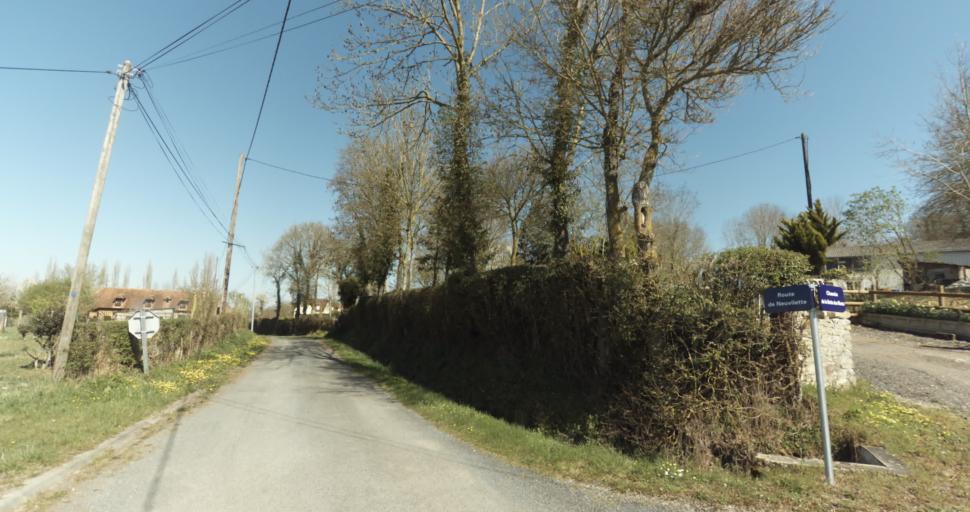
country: FR
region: Lower Normandy
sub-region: Departement du Calvados
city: Saint-Pierre-sur-Dives
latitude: 48.9590
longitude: -0.0020
